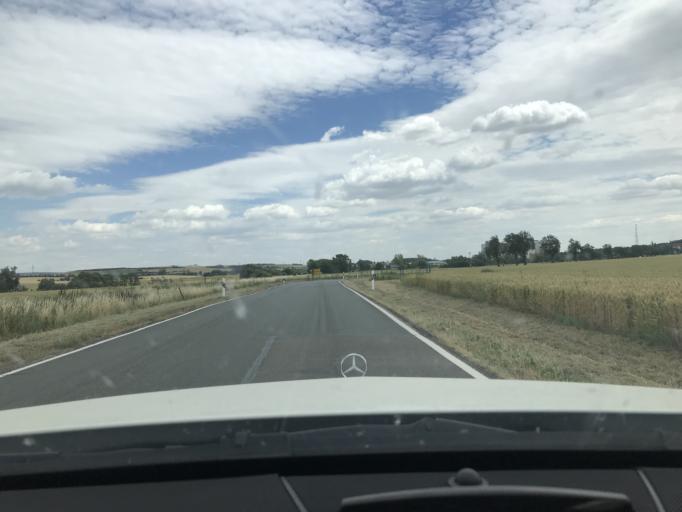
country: DE
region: Thuringia
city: Ebeleben
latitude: 51.2940
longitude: 10.7139
